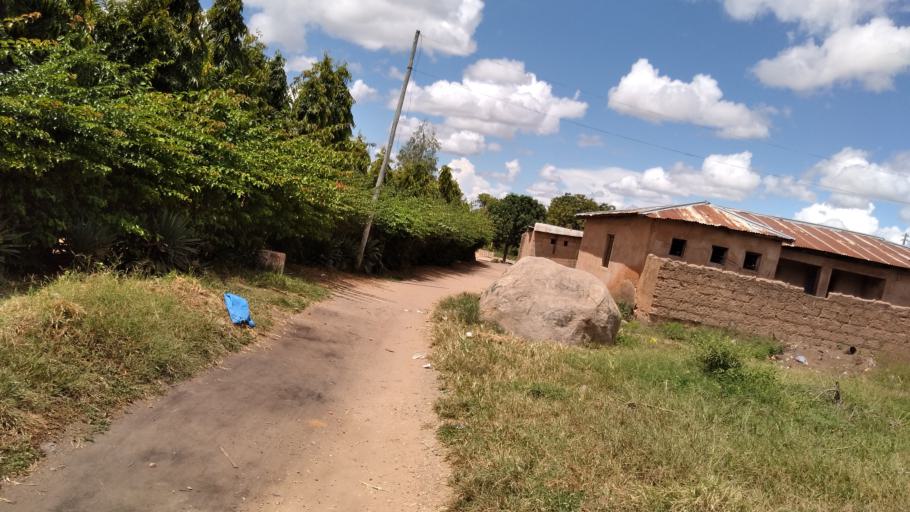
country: TZ
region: Dodoma
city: Dodoma
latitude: -6.1608
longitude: 35.7365
